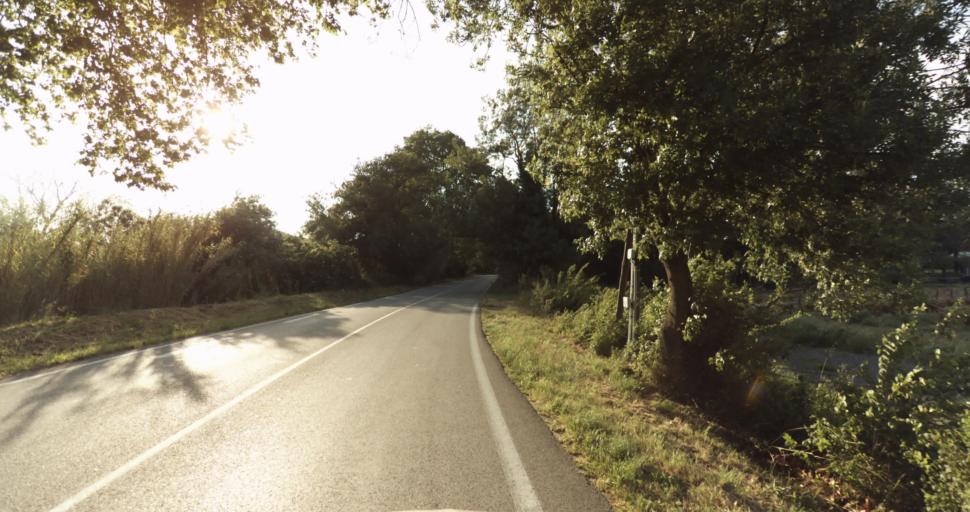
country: FR
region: Provence-Alpes-Cote d'Azur
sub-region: Departement du Var
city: Hyeres
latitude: 43.1313
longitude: 6.1652
